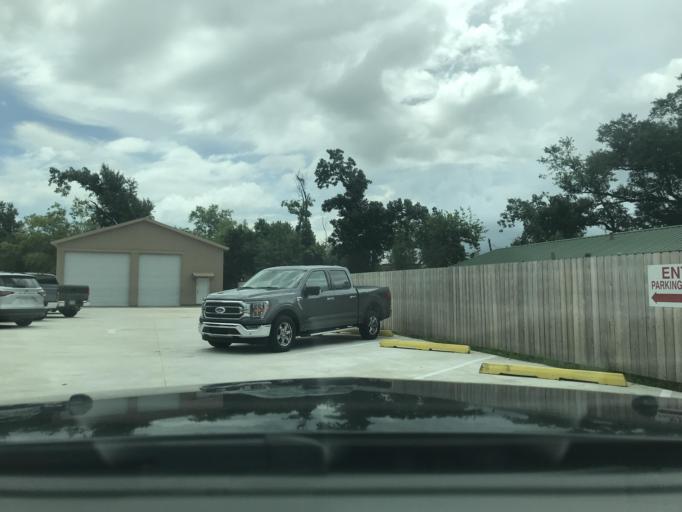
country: US
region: Louisiana
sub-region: Calcasieu Parish
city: Lake Charles
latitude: 30.2005
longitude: -93.2098
